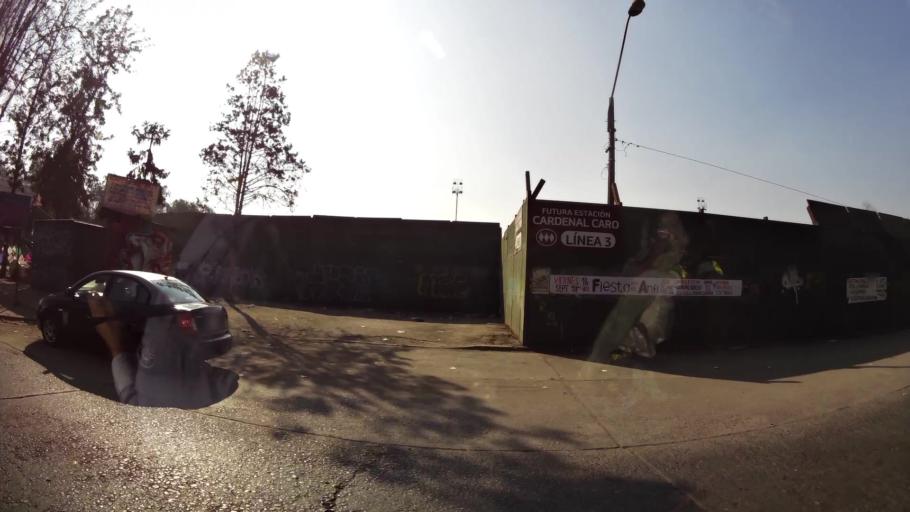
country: CL
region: Santiago Metropolitan
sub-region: Provincia de Santiago
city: Lo Prado
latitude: -33.3735
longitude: -70.6860
